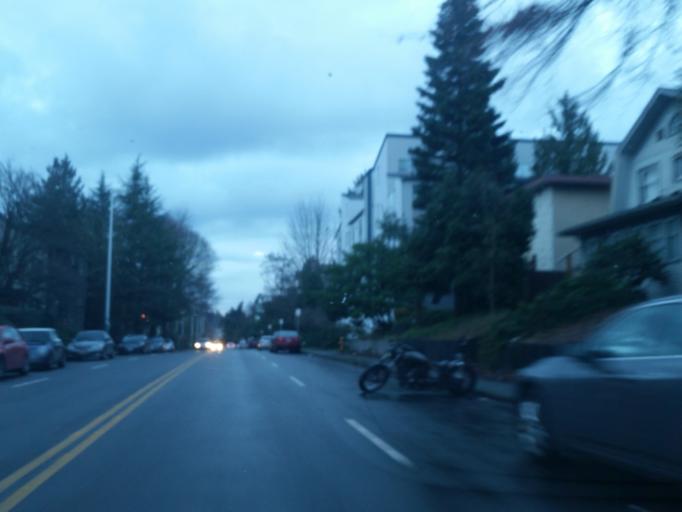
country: US
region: Washington
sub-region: King County
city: Seattle
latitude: 47.6672
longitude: -122.3119
